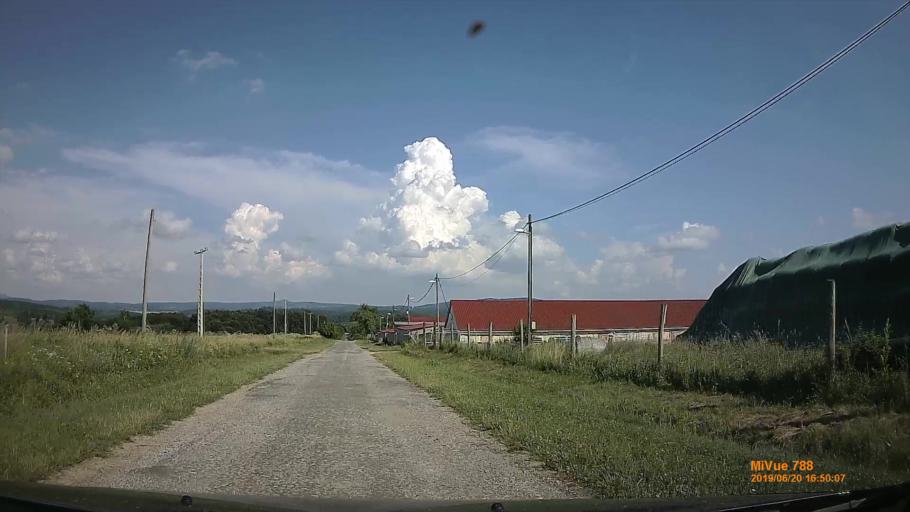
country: HU
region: Baranya
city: Buekkoesd
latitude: 46.1590
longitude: 18.0414
